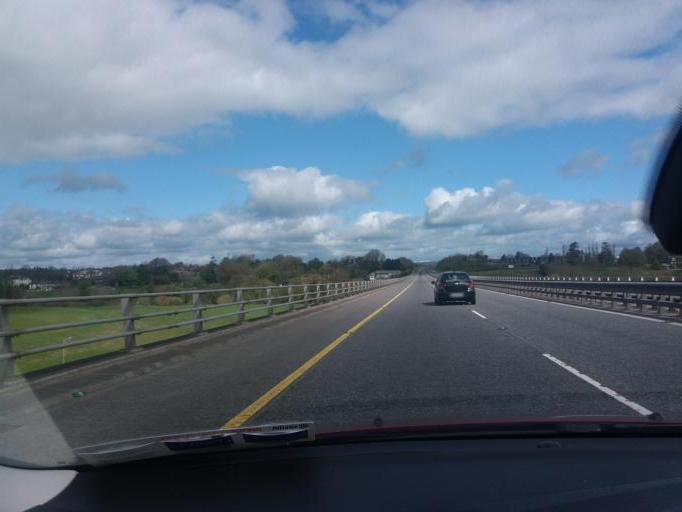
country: IE
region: Munster
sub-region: County Cork
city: Fermoy
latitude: 52.1382
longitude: -8.2614
